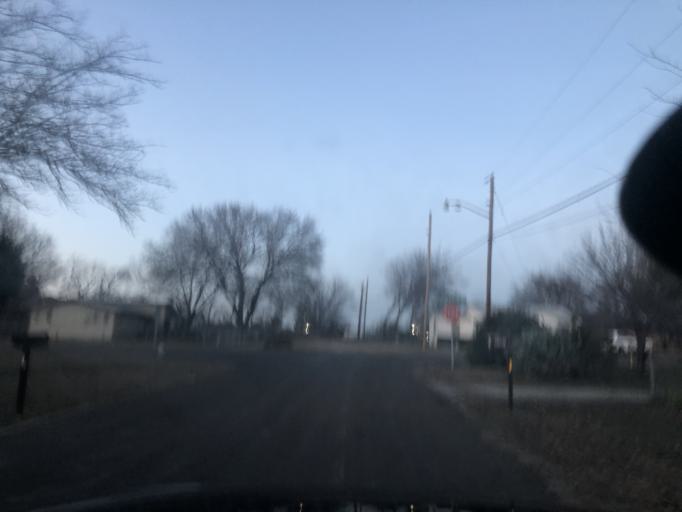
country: US
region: Texas
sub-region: Tarrant County
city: White Settlement
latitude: 32.7279
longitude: -97.4912
